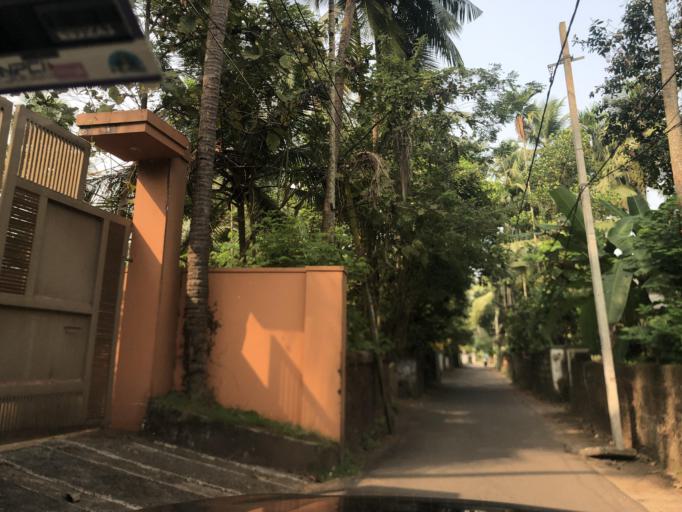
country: IN
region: Kerala
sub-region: Kozhikode
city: Kozhikode
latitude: 11.2843
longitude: 75.7769
